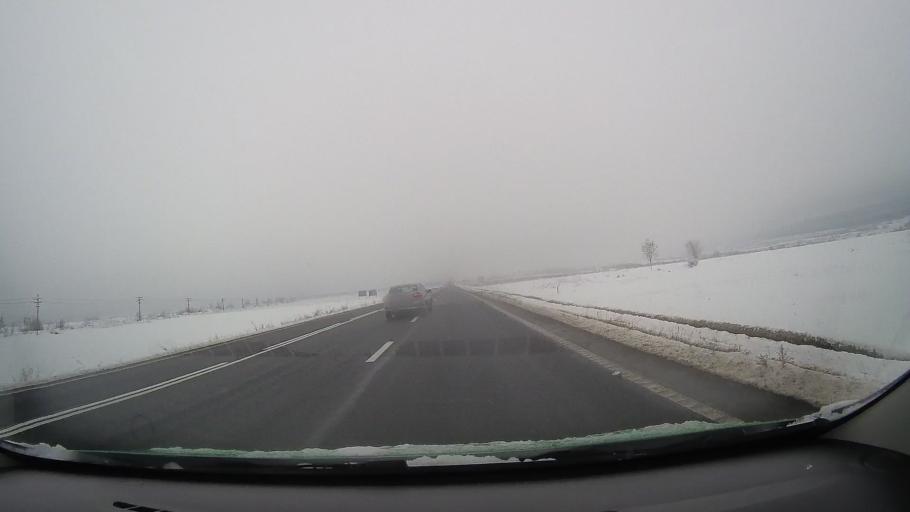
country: RO
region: Sibiu
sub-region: Oras Saliste
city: Saliste
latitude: 45.7928
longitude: 23.9180
